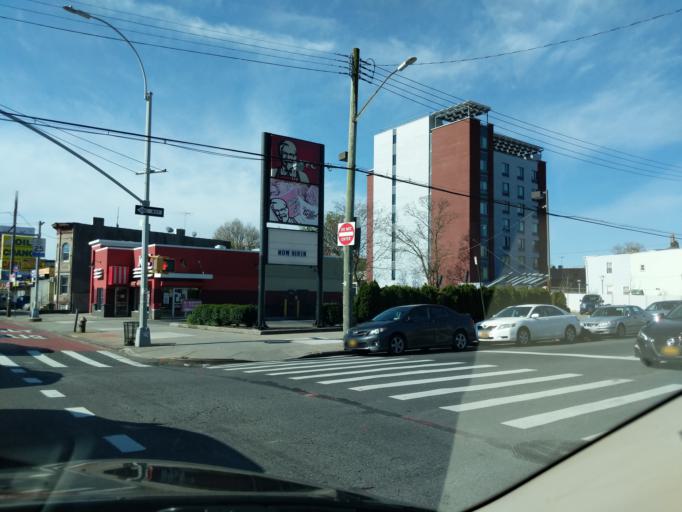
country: US
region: New York
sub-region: Kings County
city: Brooklyn
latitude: 40.6629
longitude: -73.9316
